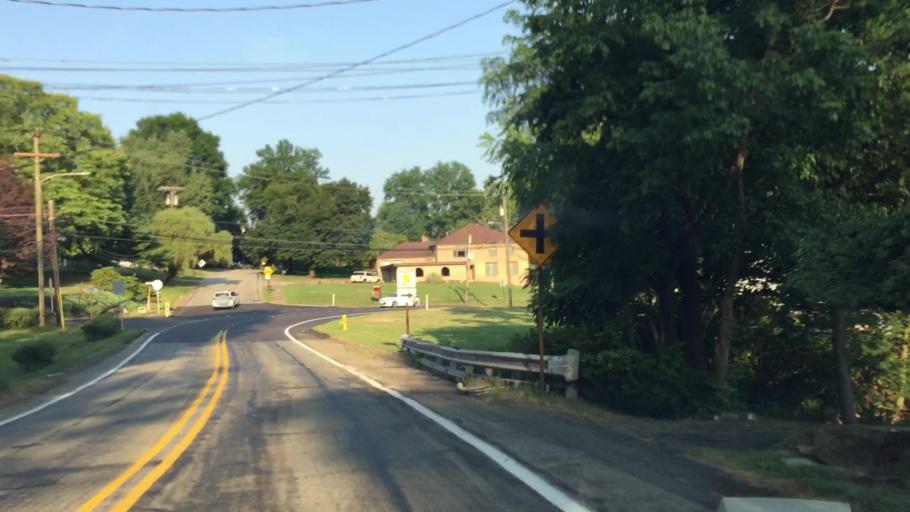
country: US
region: Pennsylvania
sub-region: Allegheny County
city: Bethel Park
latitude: 40.2994
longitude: -80.0482
